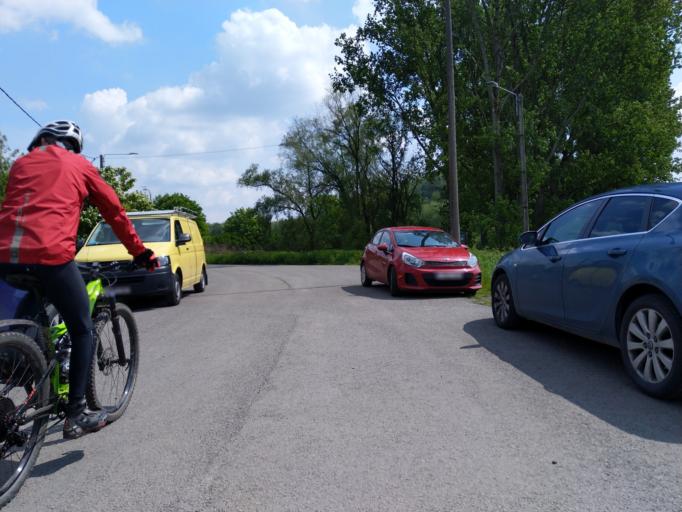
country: BE
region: Wallonia
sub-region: Province du Hainaut
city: Roeulx
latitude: 50.4728
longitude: 4.0486
